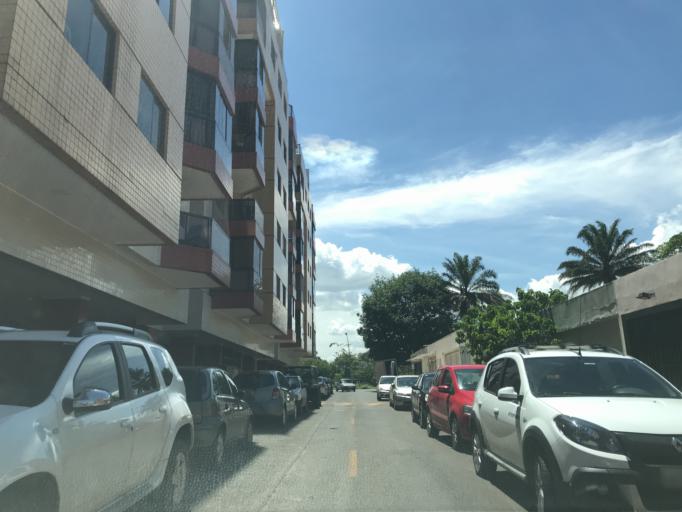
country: BR
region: Federal District
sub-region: Brasilia
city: Brasilia
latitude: -15.7760
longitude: -47.8902
